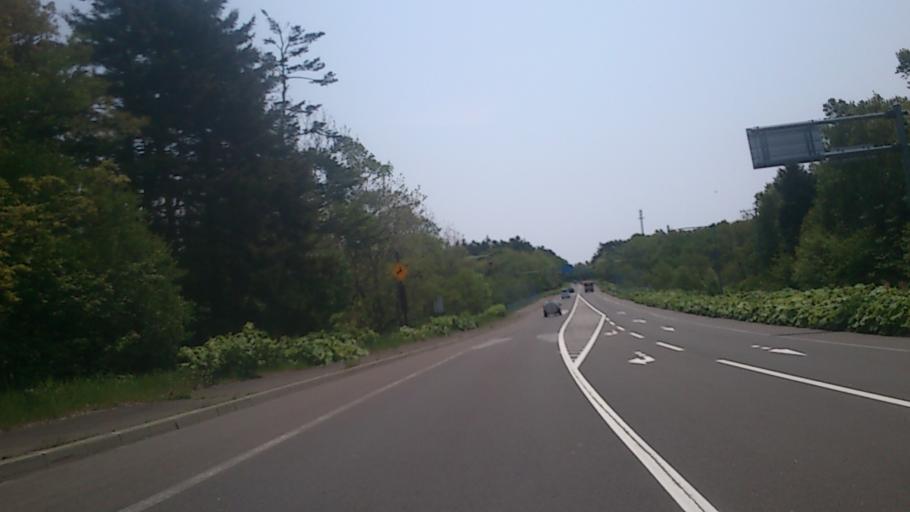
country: JP
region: Hokkaido
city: Nemuro
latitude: 43.2610
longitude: 145.4406
